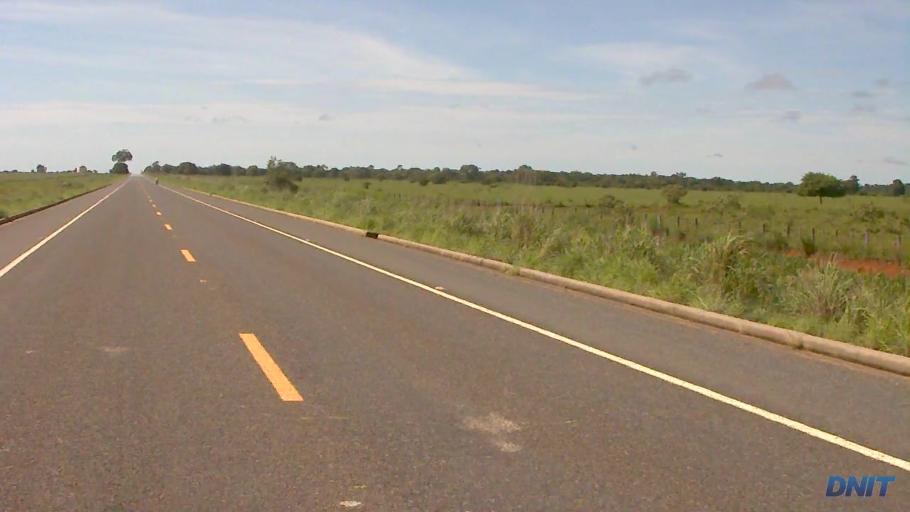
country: BR
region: Goias
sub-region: Sao Miguel Do Araguaia
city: Sao Miguel do Araguaia
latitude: -13.4181
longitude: -50.1300
